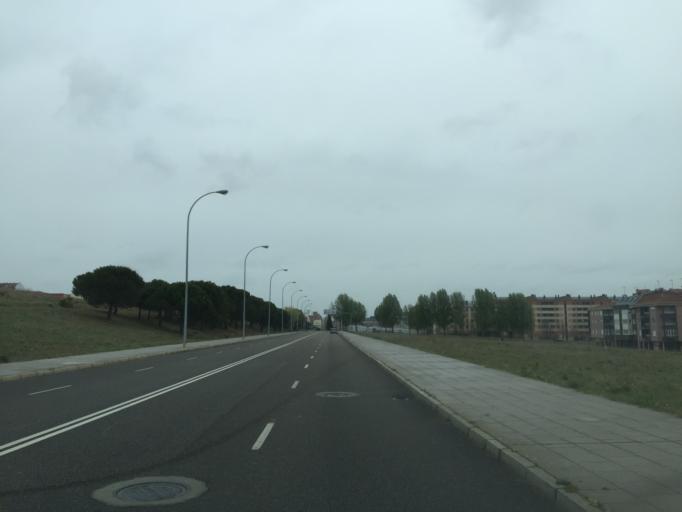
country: ES
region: Castille and Leon
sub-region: Provincia de Leon
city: Leon
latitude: 42.6153
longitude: -5.5863
